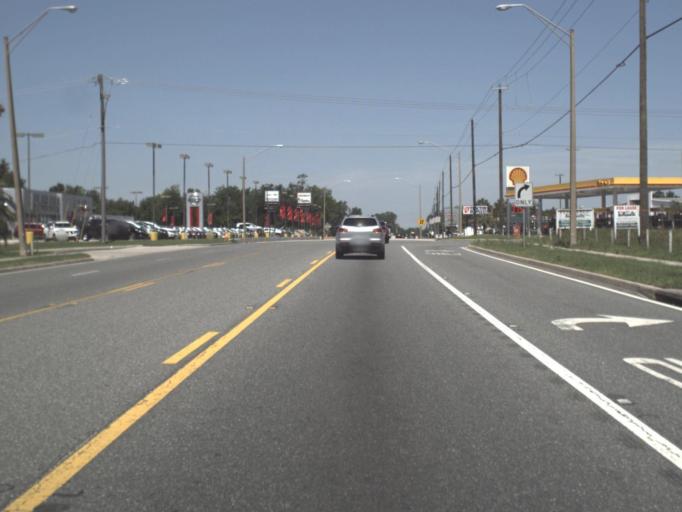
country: US
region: Florida
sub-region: Columbia County
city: Lake City
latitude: 30.1811
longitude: -82.7008
